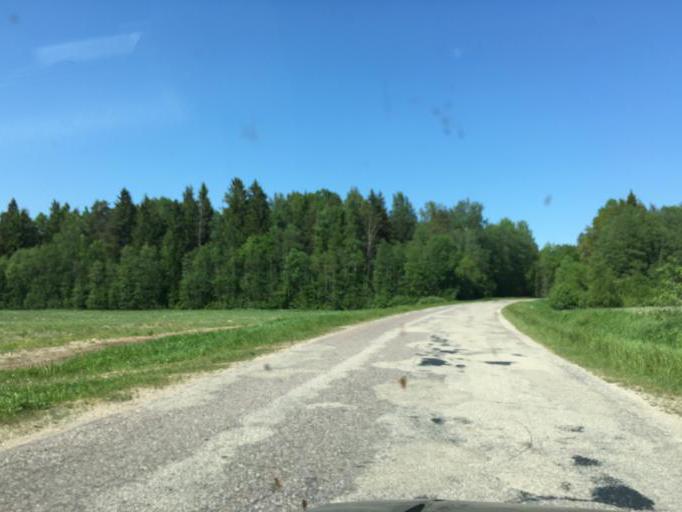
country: LV
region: Dundaga
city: Dundaga
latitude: 57.4744
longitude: 22.3226
